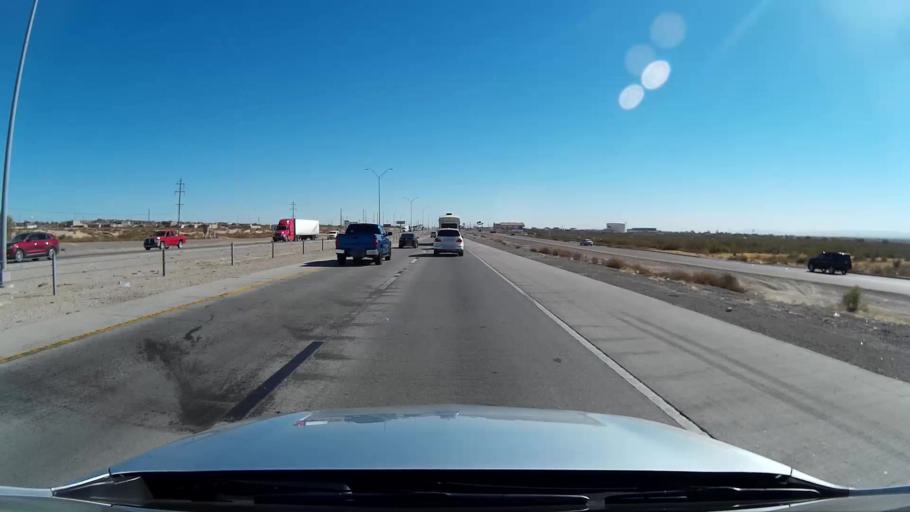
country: US
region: Texas
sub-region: El Paso County
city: Sparks
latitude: 31.6794
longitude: -106.2599
